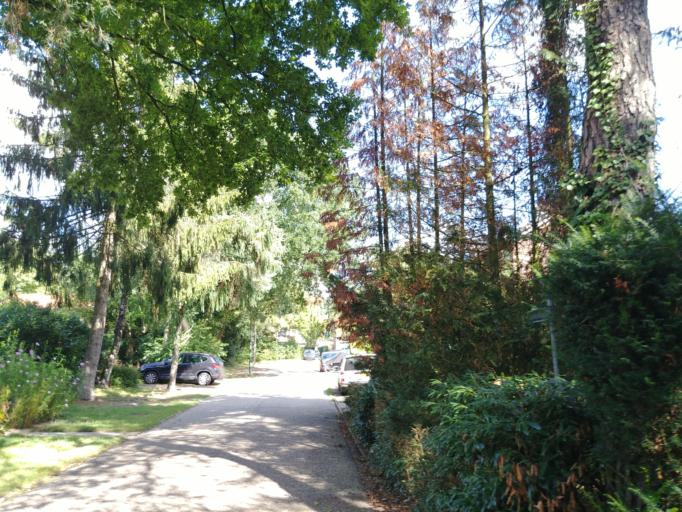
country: NL
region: Utrecht
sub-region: Gemeente Utrechtse Heuvelrug
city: Maarn
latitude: 52.0608
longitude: 5.3704
